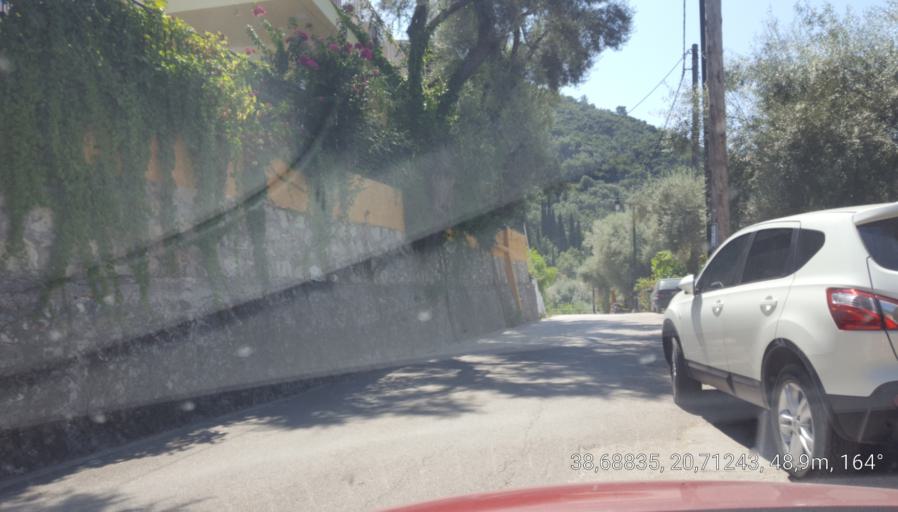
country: GR
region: Ionian Islands
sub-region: Lefkada
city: Nidri
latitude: 38.6883
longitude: 20.7125
